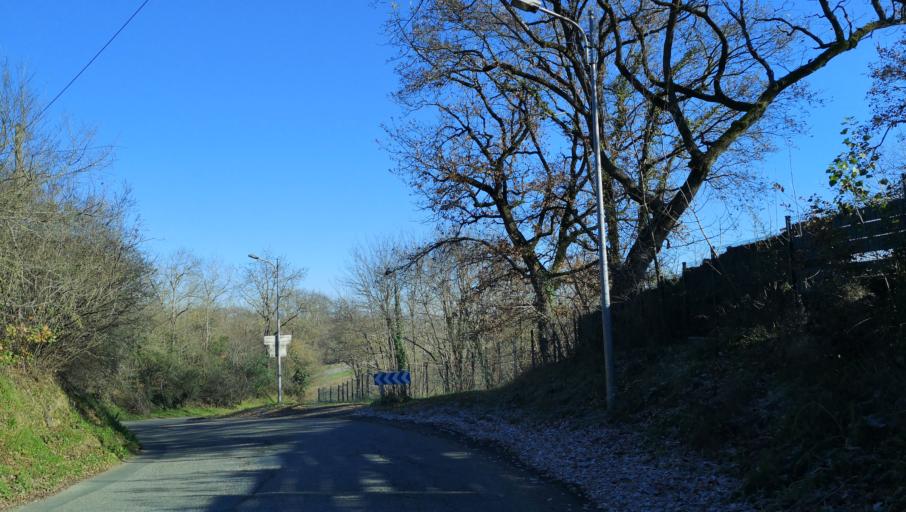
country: FR
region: Midi-Pyrenees
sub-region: Departement de la Haute-Garonne
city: Beauzelle
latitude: 43.6527
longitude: 1.3889
